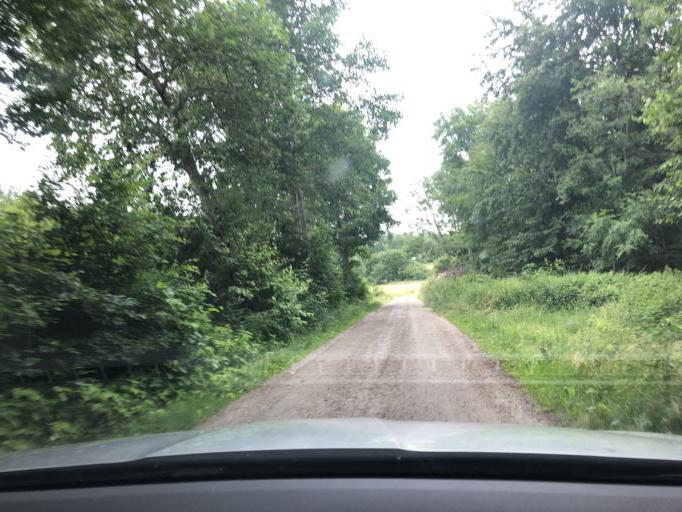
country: SE
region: Blekinge
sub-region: Solvesborgs Kommun
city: Soelvesborg
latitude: 56.1541
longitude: 14.5967
